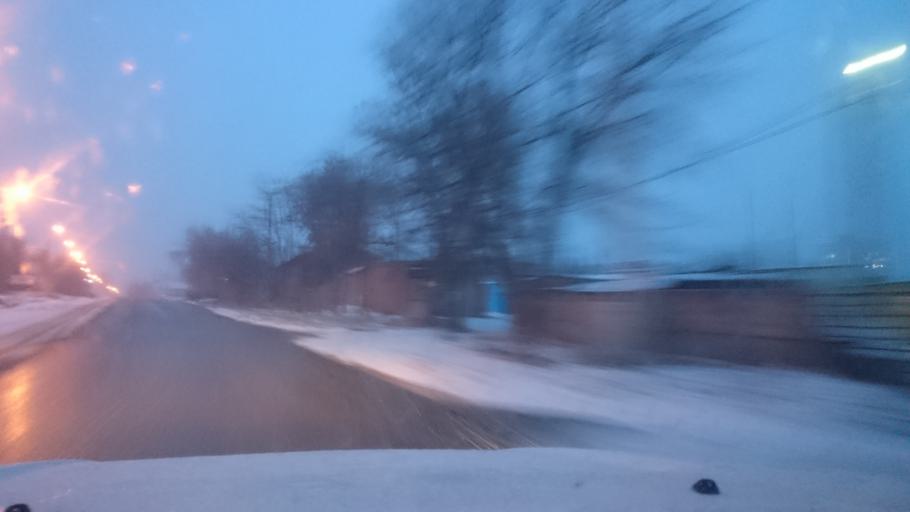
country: RU
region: Tula
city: Barsuki
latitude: 54.2041
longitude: 37.5353
